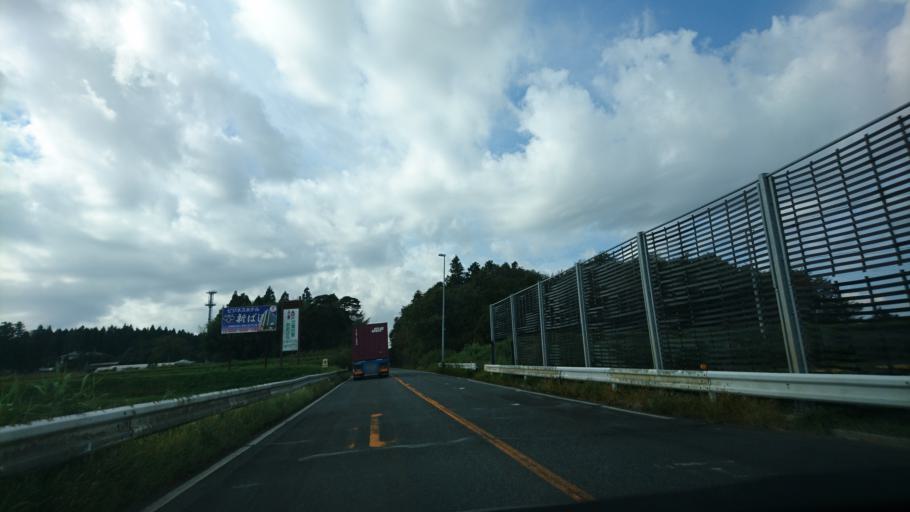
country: JP
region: Miyagi
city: Furukawa
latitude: 38.5077
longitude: 140.8925
